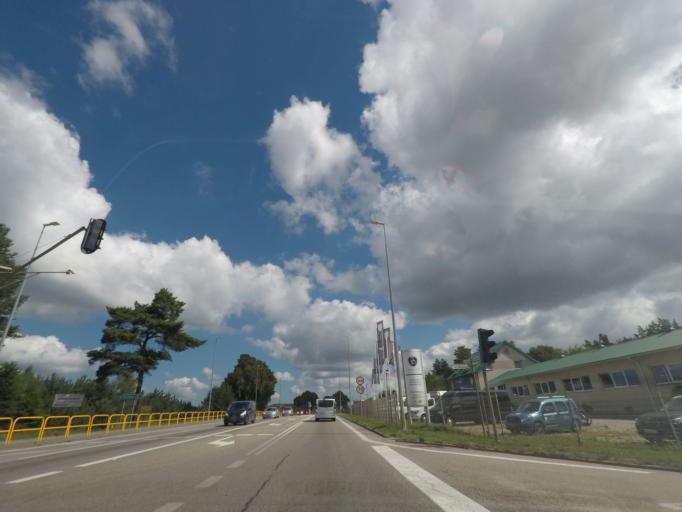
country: PL
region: Pomeranian Voivodeship
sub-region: Powiat wejherowski
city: Luzino
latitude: 54.5933
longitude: 18.1201
